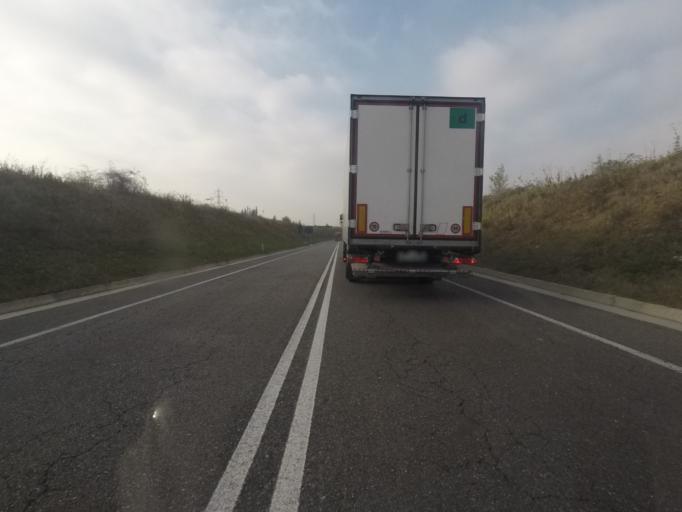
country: IT
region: Lombardy
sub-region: Provincia di Monza e Brianza
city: Burago di Molgora
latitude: 45.6079
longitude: 9.3823
